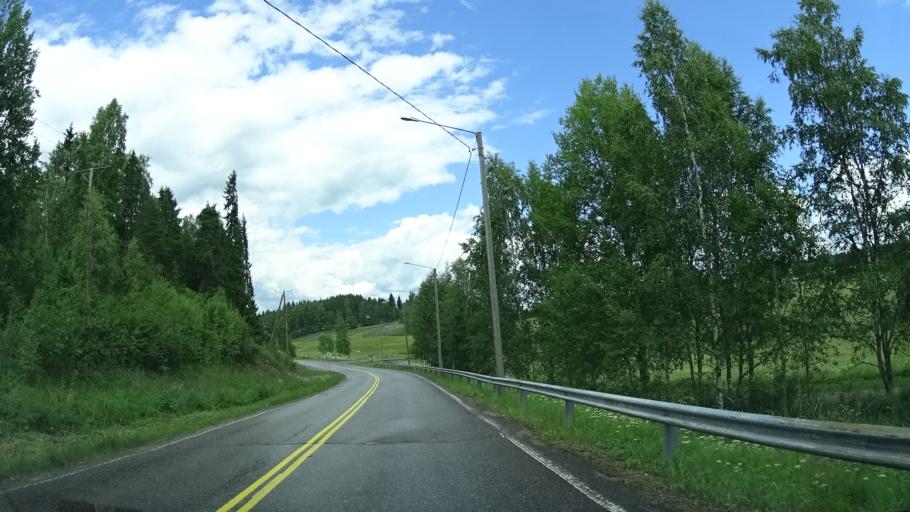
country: FI
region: Uusimaa
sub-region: Helsinki
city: Espoo
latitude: 60.3545
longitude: 24.6462
